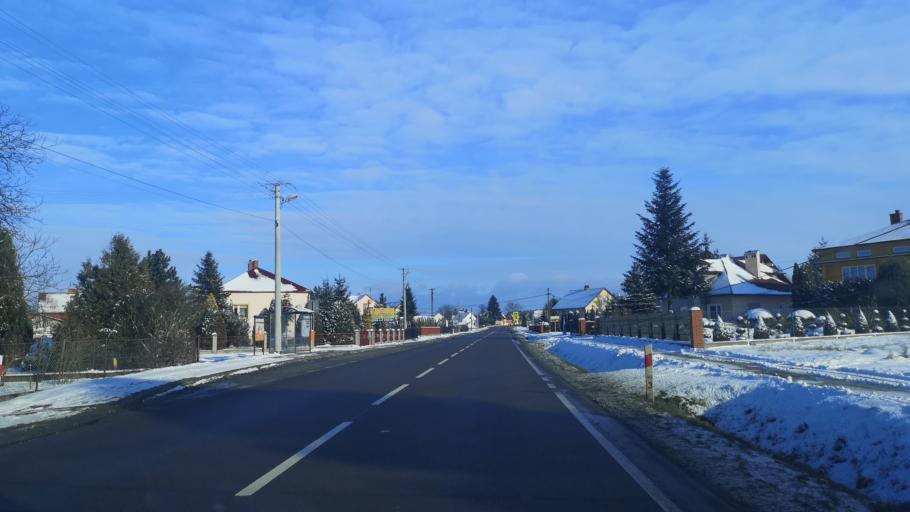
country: PL
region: Subcarpathian Voivodeship
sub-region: Powiat przeworski
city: Gorliczyna
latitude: 50.1155
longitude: 22.5086
